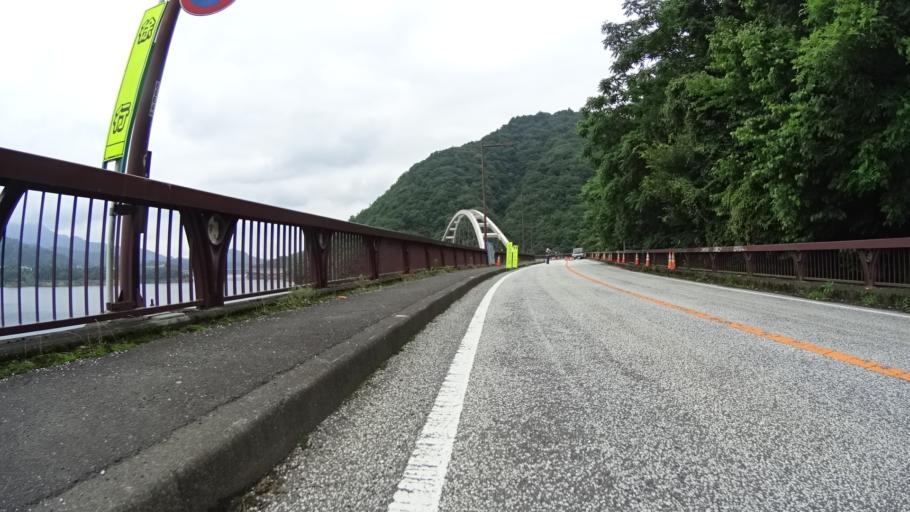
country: JP
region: Kanagawa
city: Atsugi
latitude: 35.5180
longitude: 139.2413
